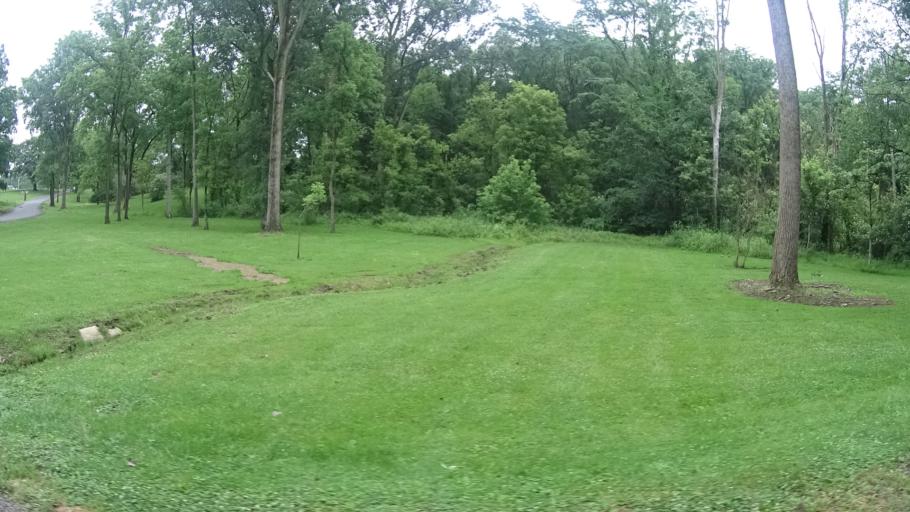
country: US
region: Ohio
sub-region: Erie County
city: Huron
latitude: 41.3556
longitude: -82.5528
